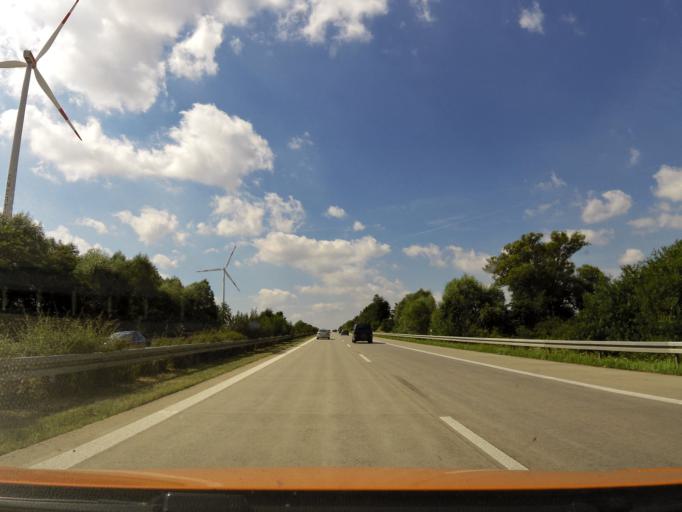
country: PL
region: West Pomeranian Voivodeship
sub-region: Powiat policki
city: Kolbaskowo
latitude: 53.3310
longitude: 14.3759
